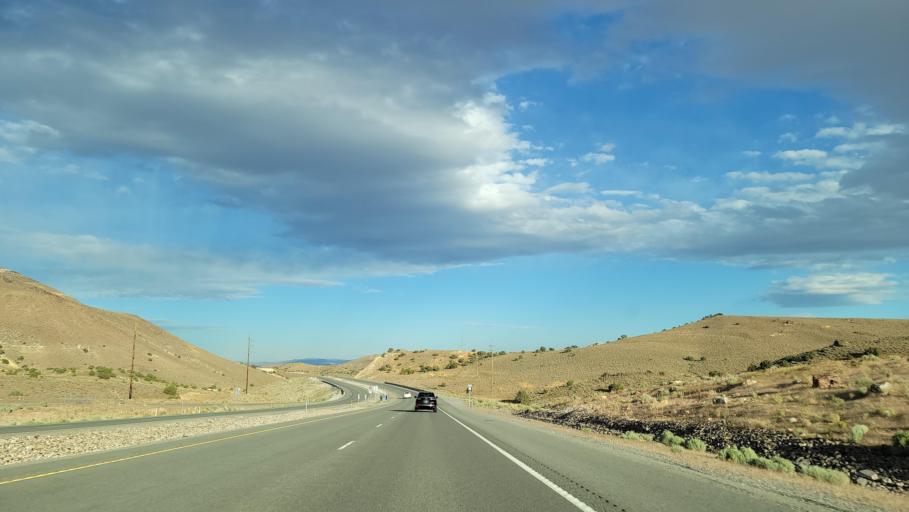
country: US
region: Nevada
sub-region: Lyon County
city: Stagecoach
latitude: 39.4714
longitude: -119.3937
